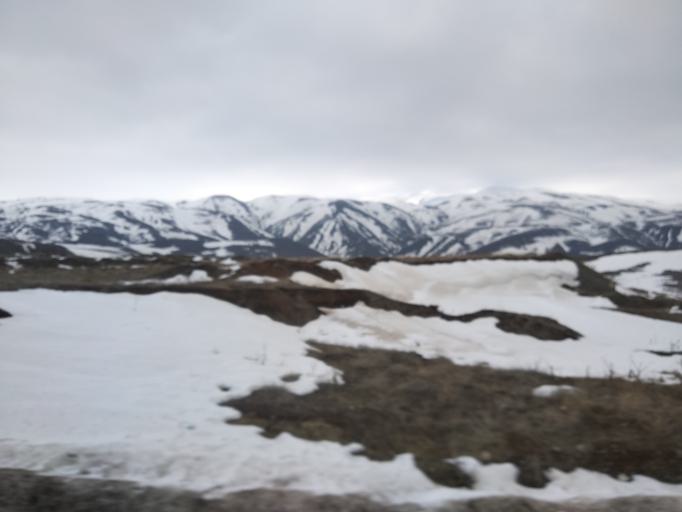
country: TR
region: Erzincan
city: Catalarmut
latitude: 39.8292
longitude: 39.3850
